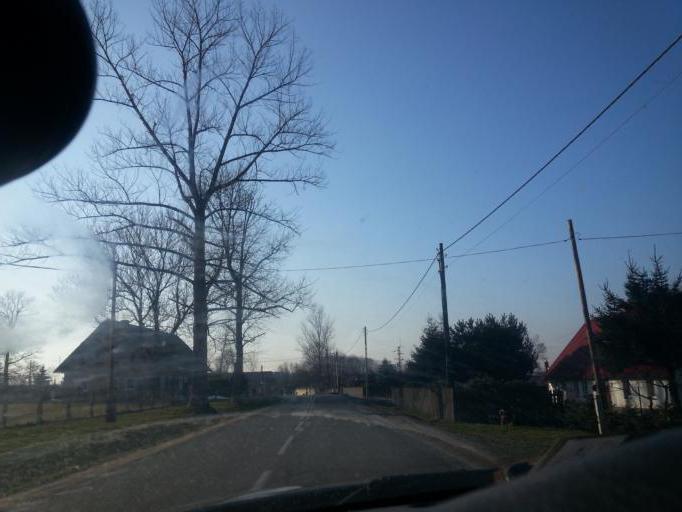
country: PL
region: Lower Silesian Voivodeship
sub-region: Powiat jeleniogorski
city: Myslakowice
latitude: 50.8268
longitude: 15.7982
